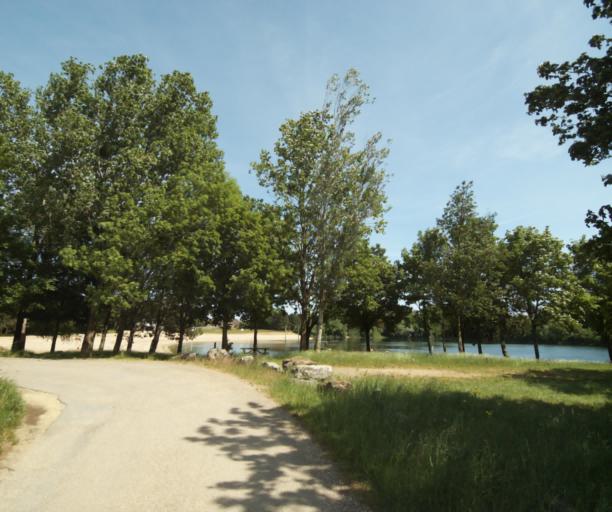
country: FR
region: Champagne-Ardenne
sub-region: Departement des Ardennes
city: Prix-les-Mezieres
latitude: 49.7601
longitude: 4.6821
